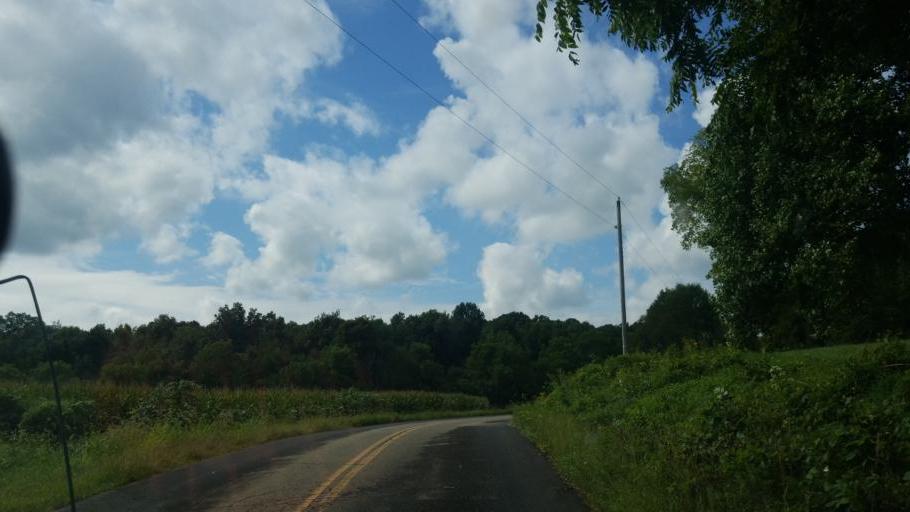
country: US
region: Ohio
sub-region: Knox County
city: Mount Vernon
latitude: 40.4508
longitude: -82.4549
